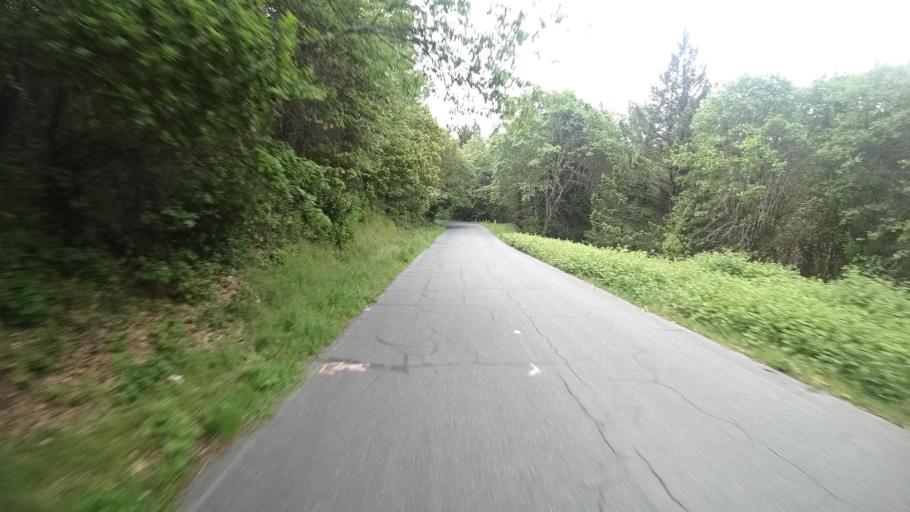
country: US
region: California
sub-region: Humboldt County
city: Willow Creek
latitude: 41.1047
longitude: -123.7113
